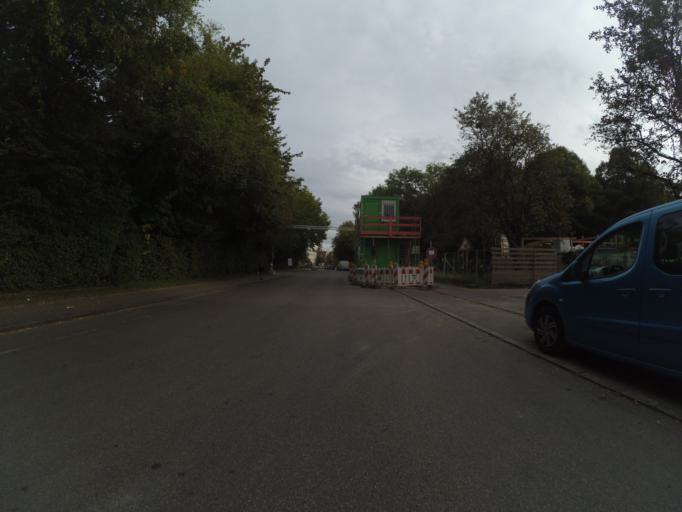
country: DE
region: Bavaria
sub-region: Upper Bavaria
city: Munich
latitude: 48.1637
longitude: 11.5204
